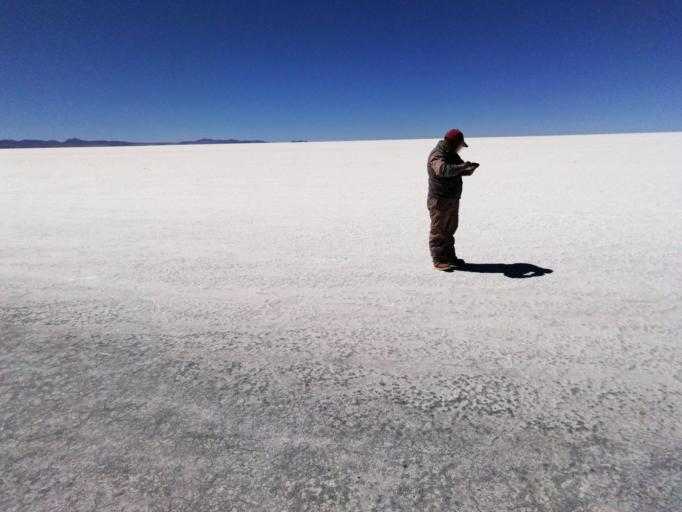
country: BO
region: Potosi
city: Colchani
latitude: -20.3223
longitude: -67.0015
